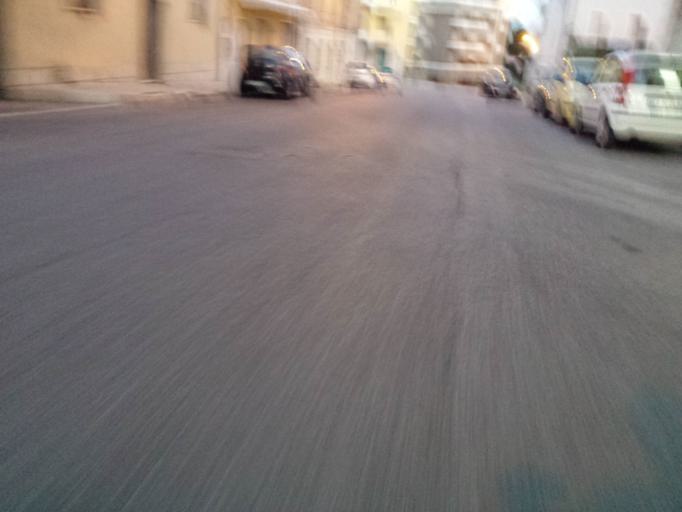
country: IT
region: Molise
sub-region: Provincia di Campobasso
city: Campobasso
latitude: 41.5650
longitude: 14.6731
